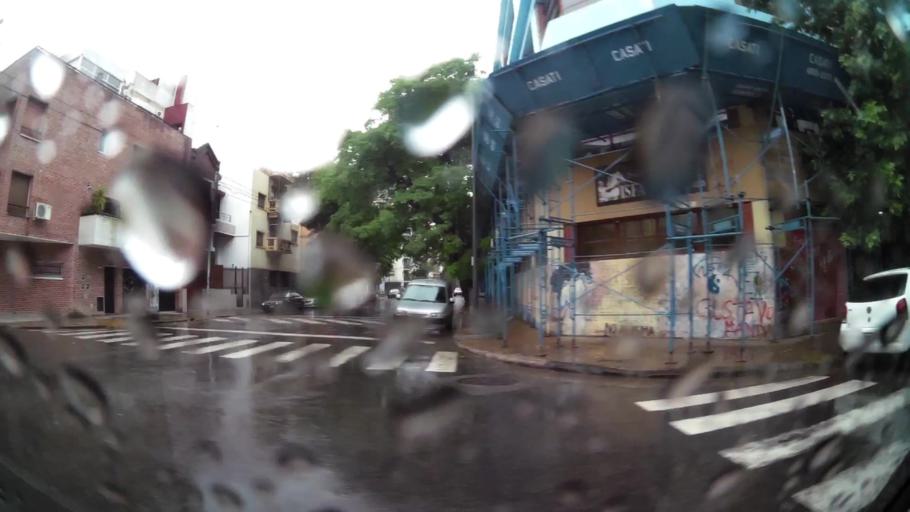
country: AR
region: Buenos Aires F.D.
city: Buenos Aires
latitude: -34.6349
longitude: -58.3721
